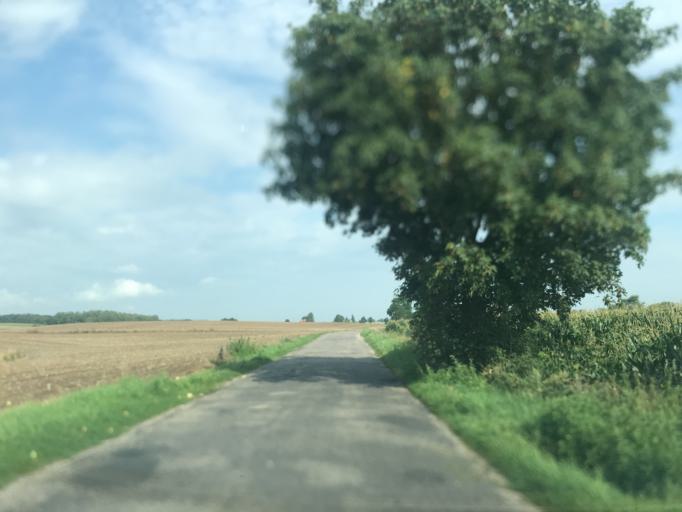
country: PL
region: Kujawsko-Pomorskie
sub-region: Powiat brodnicki
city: Brzozie
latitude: 53.3621
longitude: 19.5932
